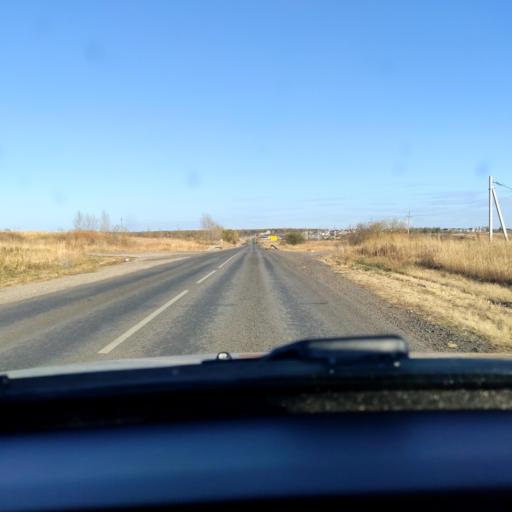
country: RU
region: Voronezj
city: Semiluki
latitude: 51.7242
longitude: 39.0035
